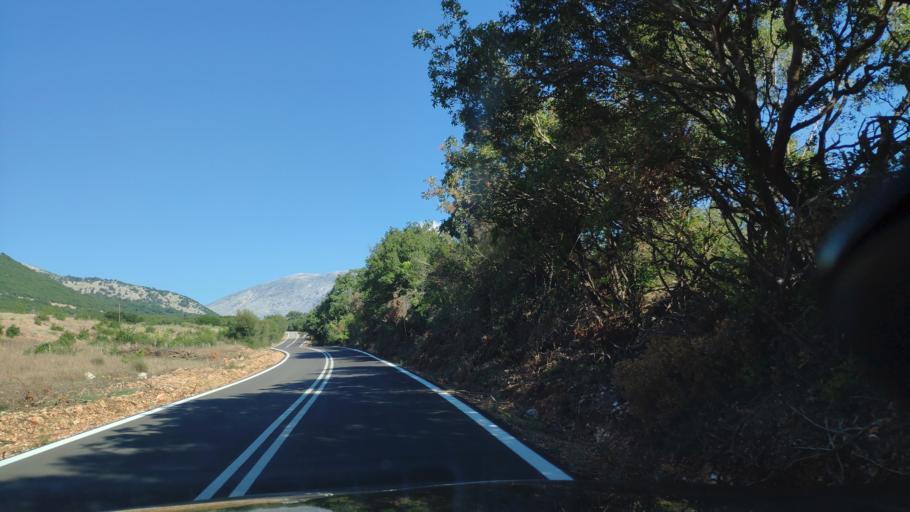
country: GR
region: West Greece
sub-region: Nomos Aitolias kai Akarnanias
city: Fitiai
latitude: 38.6813
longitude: 21.1297
